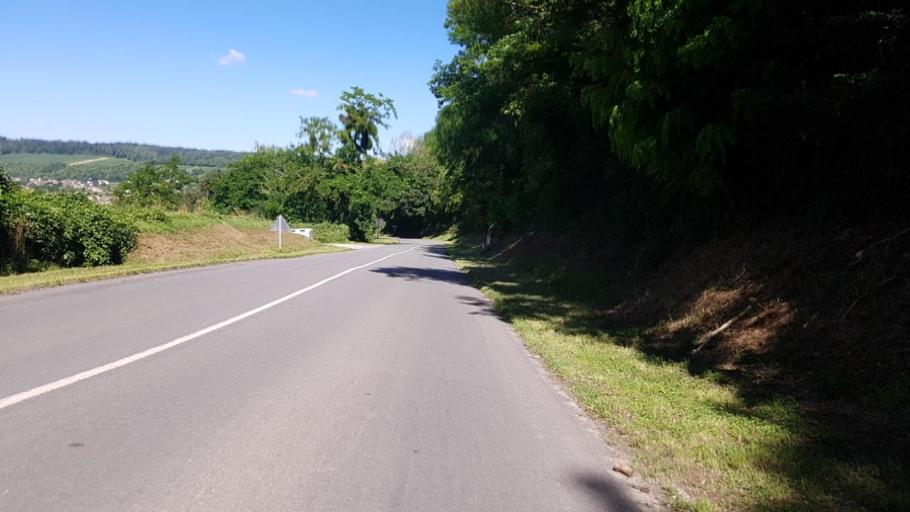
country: FR
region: Picardie
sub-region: Departement de l'Aisne
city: Charly-sur-Marne
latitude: 48.9784
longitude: 3.2472
